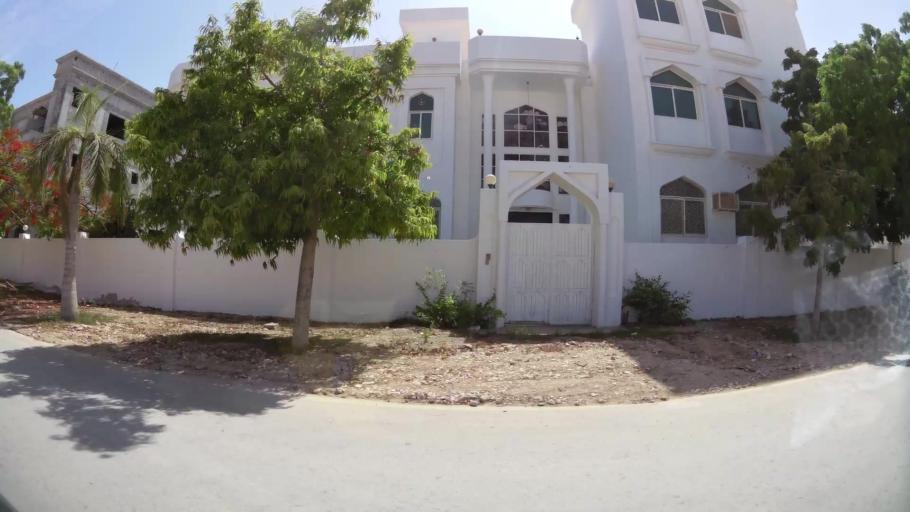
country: OM
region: Zufar
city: Salalah
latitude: 17.0422
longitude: 54.1495
